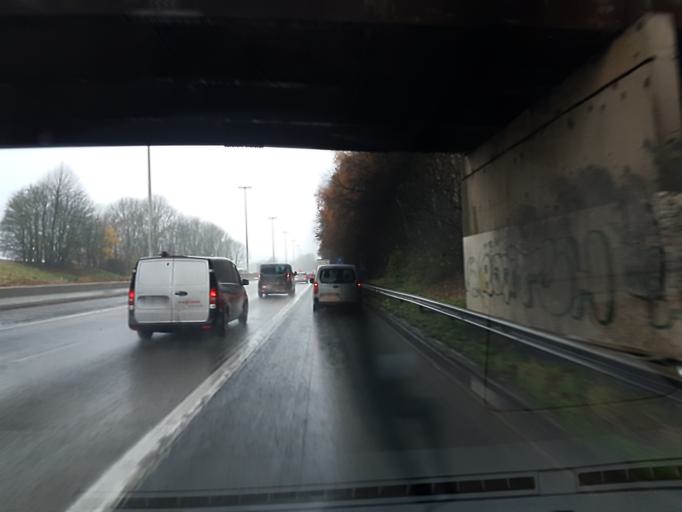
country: BE
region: Wallonia
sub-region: Province de Namur
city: Noville-les-Bois
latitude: 50.5320
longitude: 5.0311
